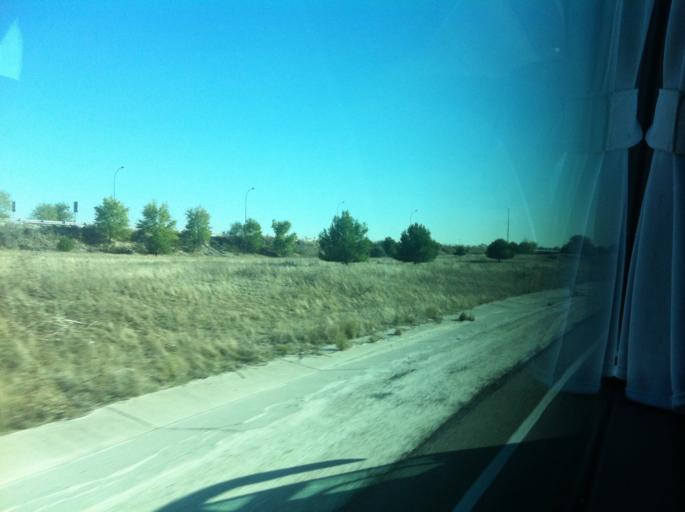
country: ES
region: Madrid
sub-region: Provincia de Madrid
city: San Sebastian de los Reyes
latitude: 40.5438
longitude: -3.5725
